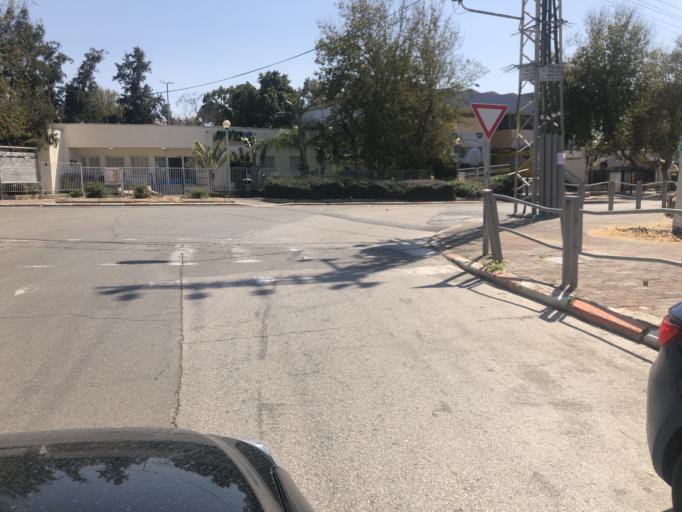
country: IL
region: Tel Aviv
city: Holon
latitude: 32.0045
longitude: 34.7634
